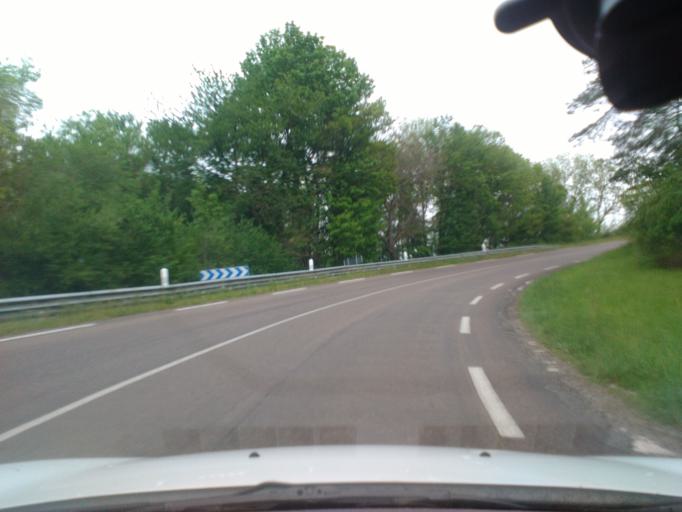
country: FR
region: Champagne-Ardenne
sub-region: Departement de l'Aube
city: Bar-sur-Aube
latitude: 48.2259
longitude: 4.7553
